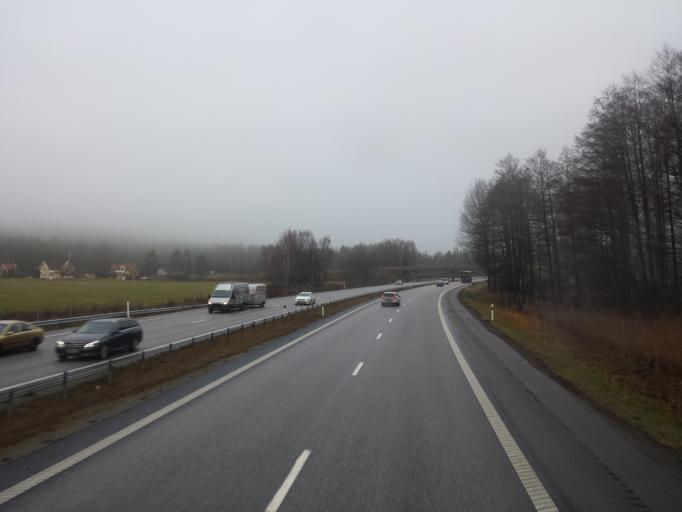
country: SE
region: OEstergoetland
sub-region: Norrkopings Kommun
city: Krokek
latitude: 58.7008
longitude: 16.3401
